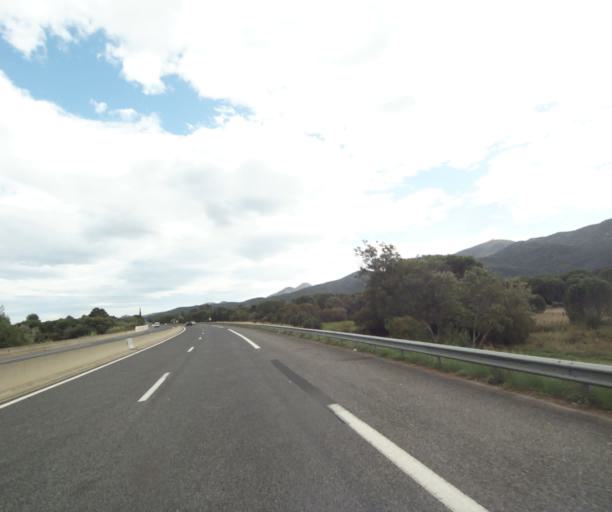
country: FR
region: Languedoc-Roussillon
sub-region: Departement des Pyrenees-Orientales
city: Argelers
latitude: 42.5433
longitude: 3.0112
